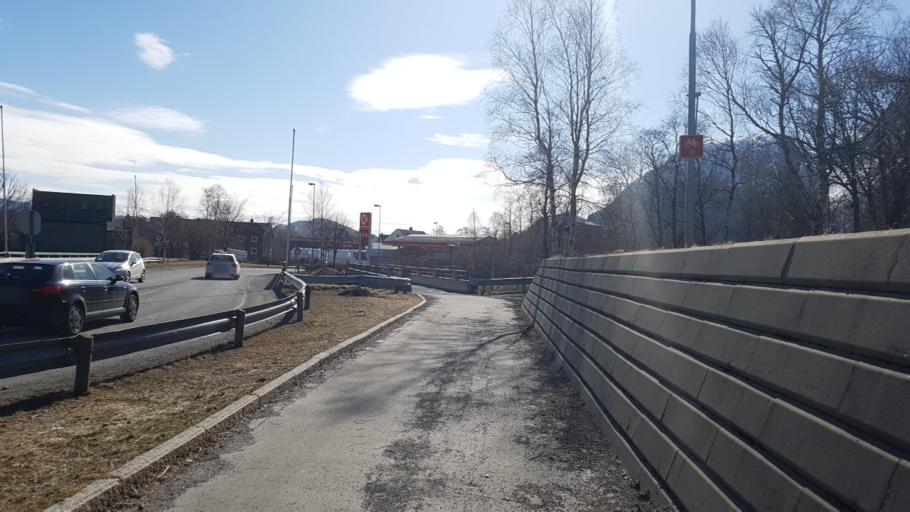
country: NO
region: Nordland
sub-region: Vefsn
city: Mosjoen
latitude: 65.8430
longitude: 13.2010
